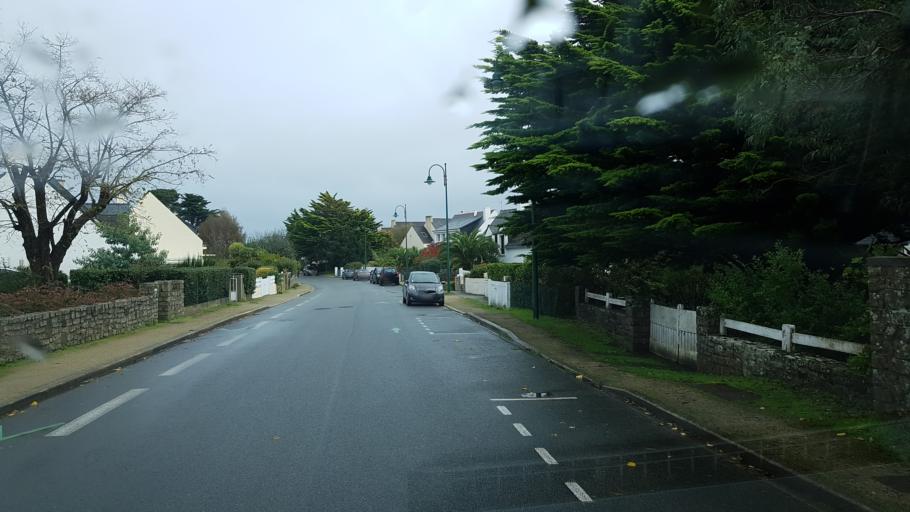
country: FR
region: Brittany
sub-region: Departement du Morbihan
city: Arzon
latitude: 47.5484
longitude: -2.9010
